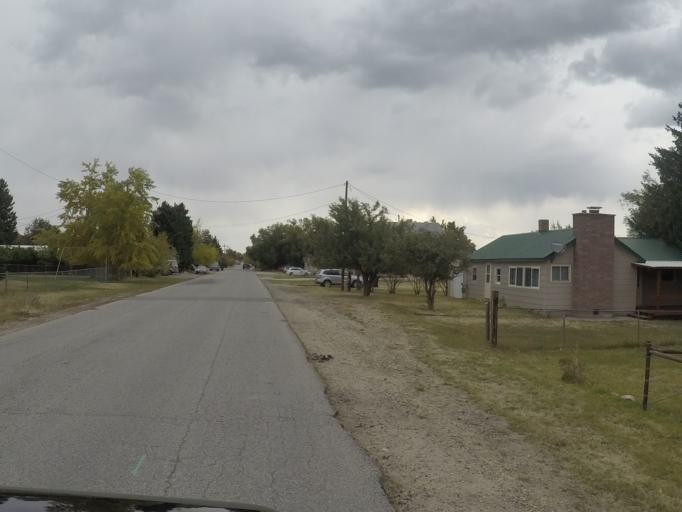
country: US
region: Montana
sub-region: Carbon County
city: Red Lodge
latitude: 45.1933
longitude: -109.2445
